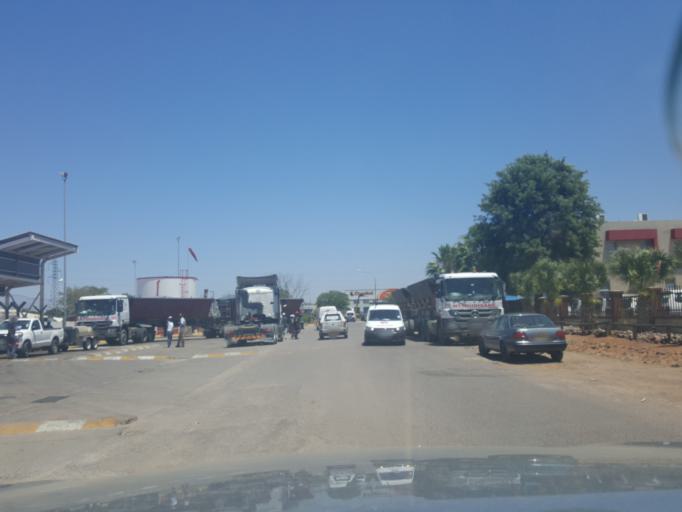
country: BW
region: South East
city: Gaborone
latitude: -24.6881
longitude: 25.8869
